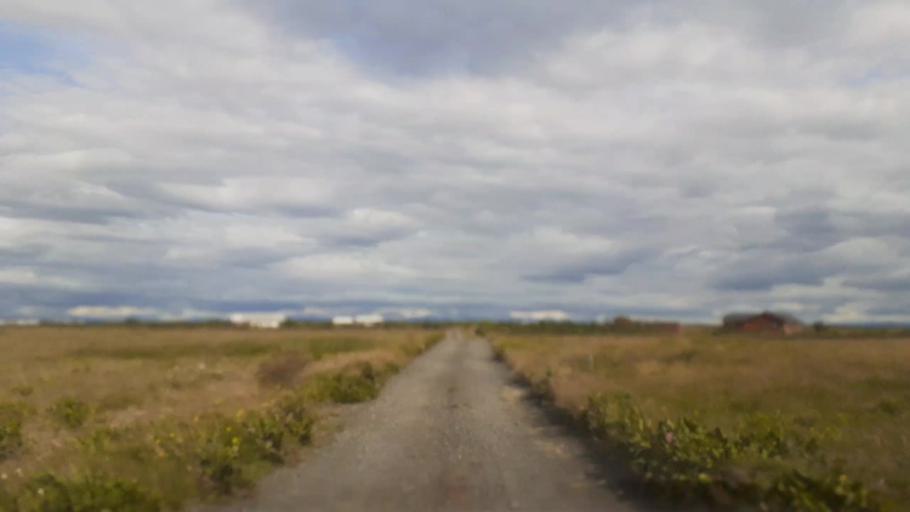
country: IS
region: South
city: Vestmannaeyjar
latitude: 63.7705
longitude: -20.2973
